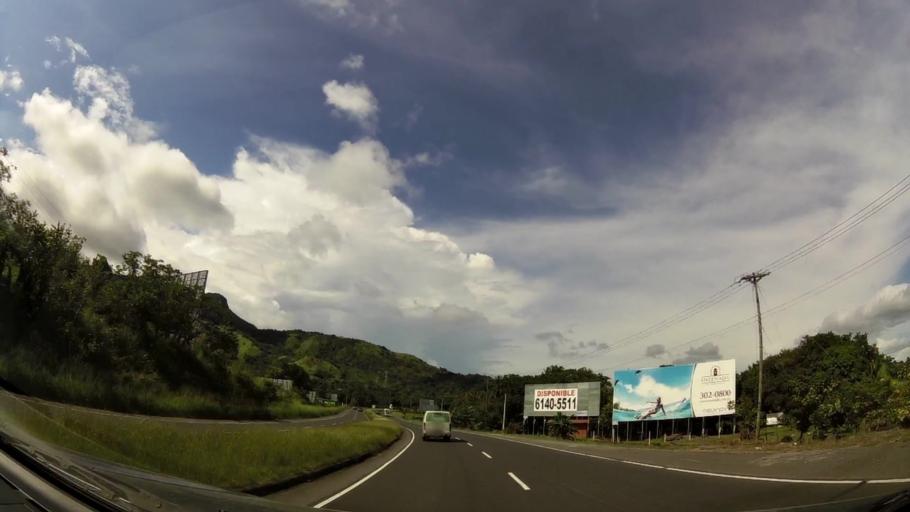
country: PA
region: Panama
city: Bejuco
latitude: 8.6571
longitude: -79.8712
